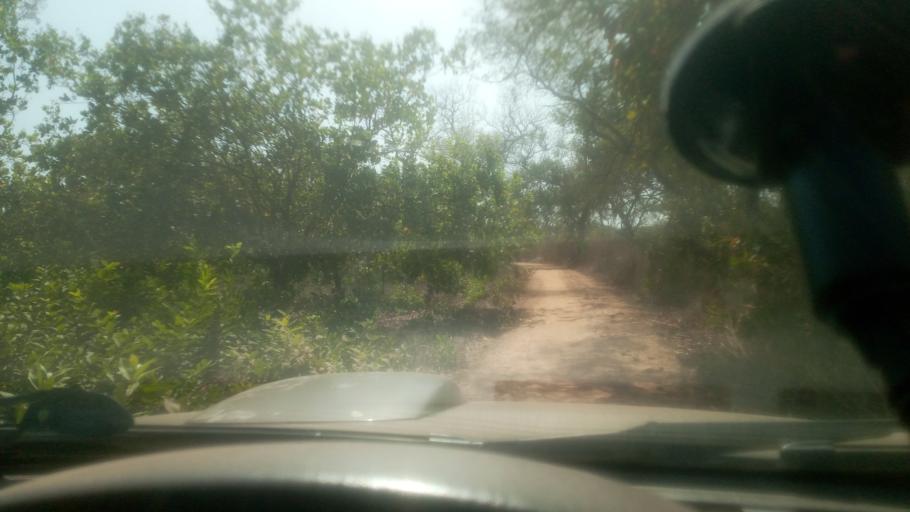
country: GW
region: Oio
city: Farim
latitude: 12.4540
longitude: -15.4117
